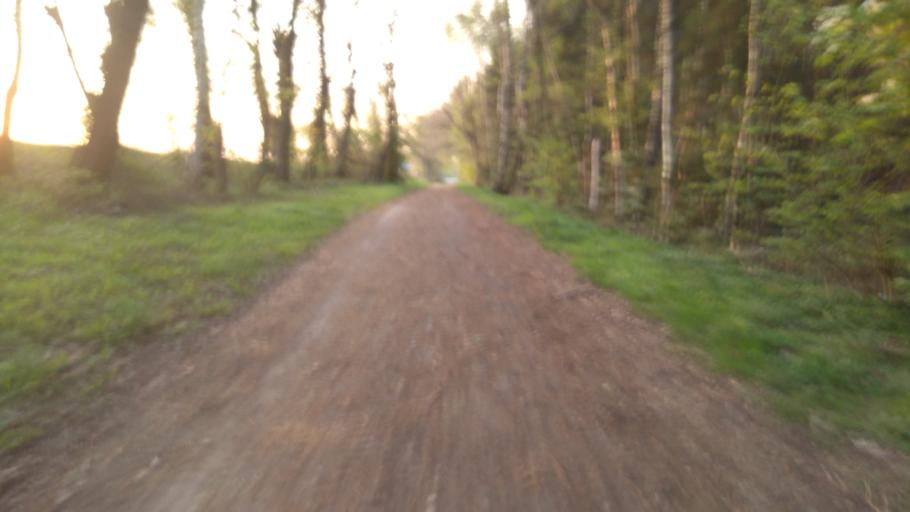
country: DE
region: Lower Saxony
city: Harsefeld
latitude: 53.4783
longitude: 9.5203
